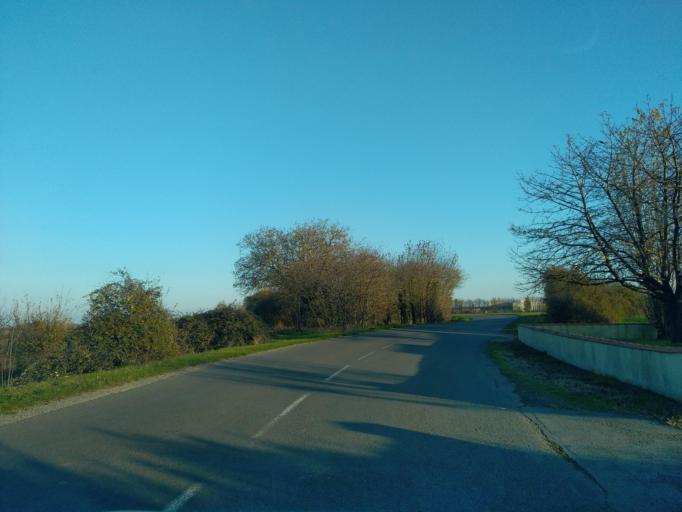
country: FR
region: Pays de la Loire
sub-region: Departement de la Vendee
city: Maillezais
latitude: 46.3411
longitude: -0.7757
